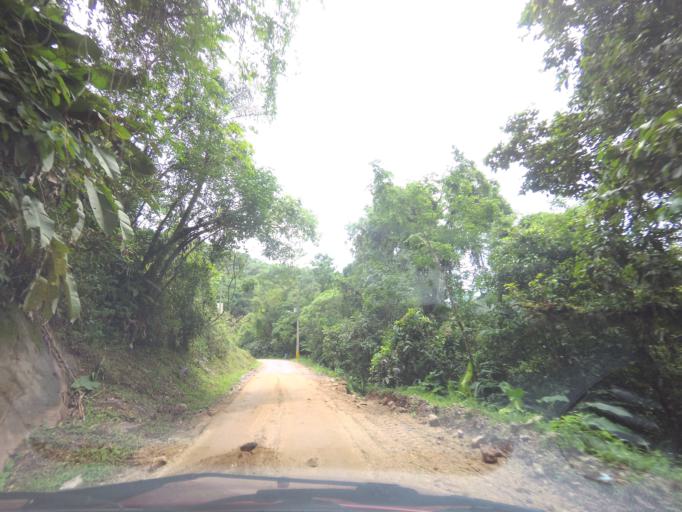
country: BR
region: Santa Catarina
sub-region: Blumenau
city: Blumenau
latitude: -26.9826
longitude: -49.0280
